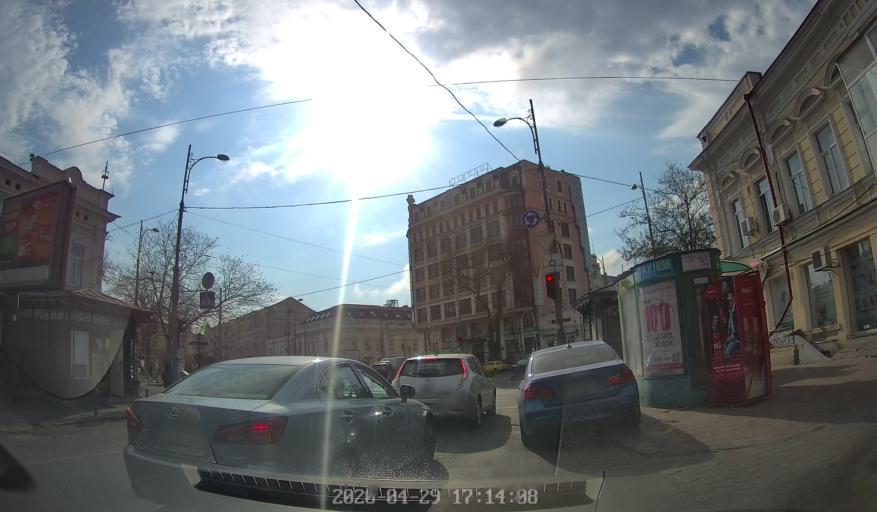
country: GR
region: South Aegean
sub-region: Nomos Kykladon
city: Serifos
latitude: 37.1841
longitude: 24.5859
